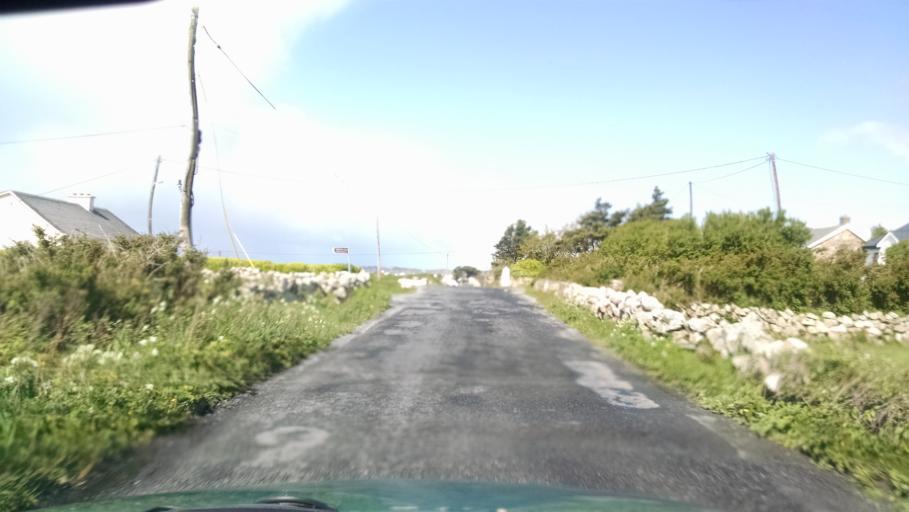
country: IE
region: Connaught
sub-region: County Galway
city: Oughterard
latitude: 53.2440
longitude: -9.5222
